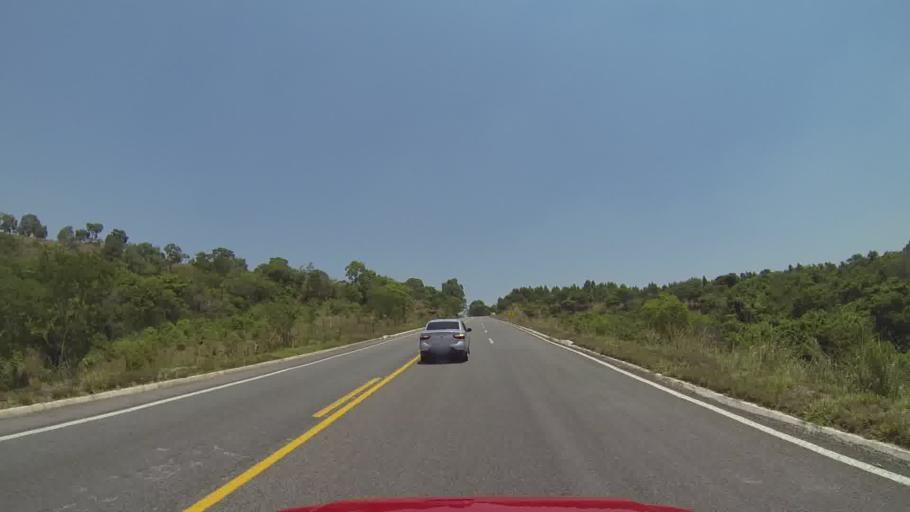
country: BR
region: Minas Gerais
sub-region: Itapecerica
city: Itapecerica
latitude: -20.2781
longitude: -45.1263
